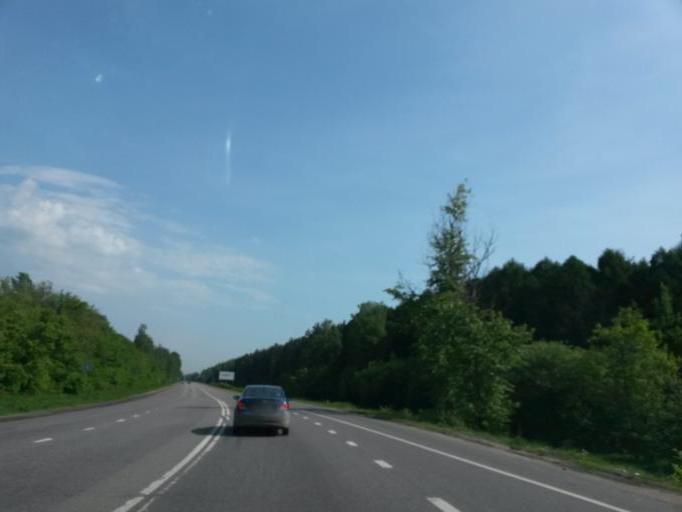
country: RU
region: Moskovskaya
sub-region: Chekhovskiy Rayon
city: Chekhov
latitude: 55.1895
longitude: 37.5014
